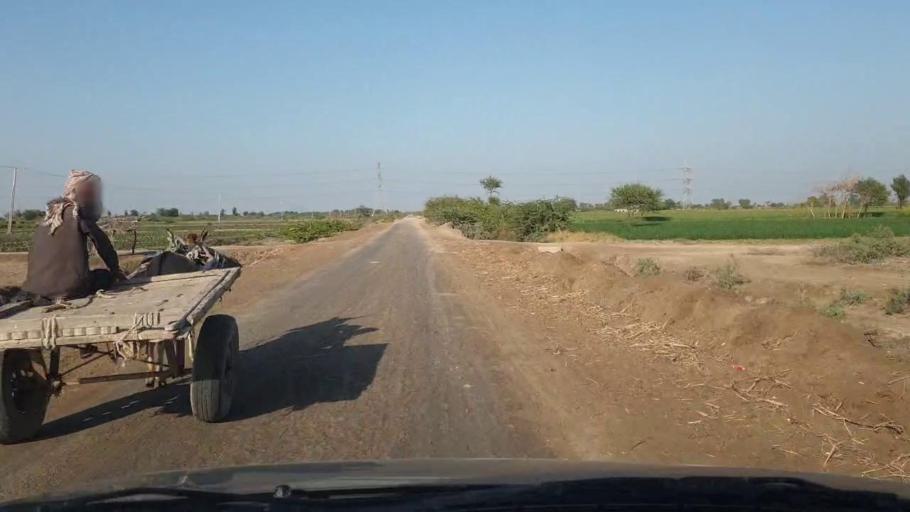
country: PK
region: Sindh
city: Samaro
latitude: 25.1480
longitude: 69.3077
